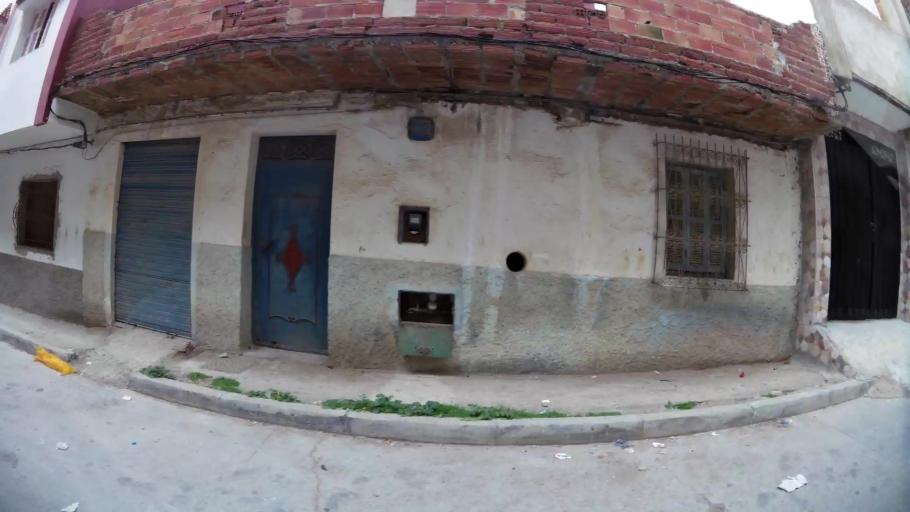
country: MA
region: Tanger-Tetouan
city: Tetouan
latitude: 35.5685
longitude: -5.3943
